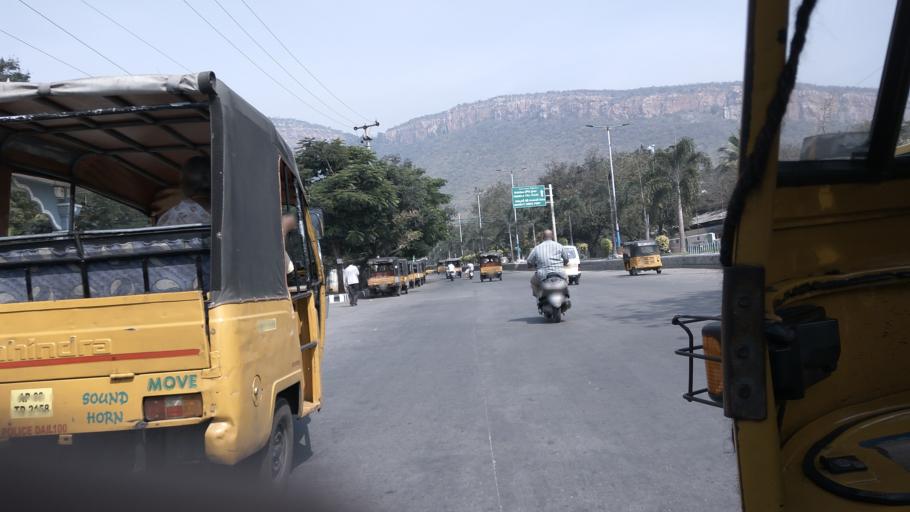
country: IN
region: Andhra Pradesh
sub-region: Chittoor
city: Tirupati
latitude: 13.6425
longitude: 79.4090
